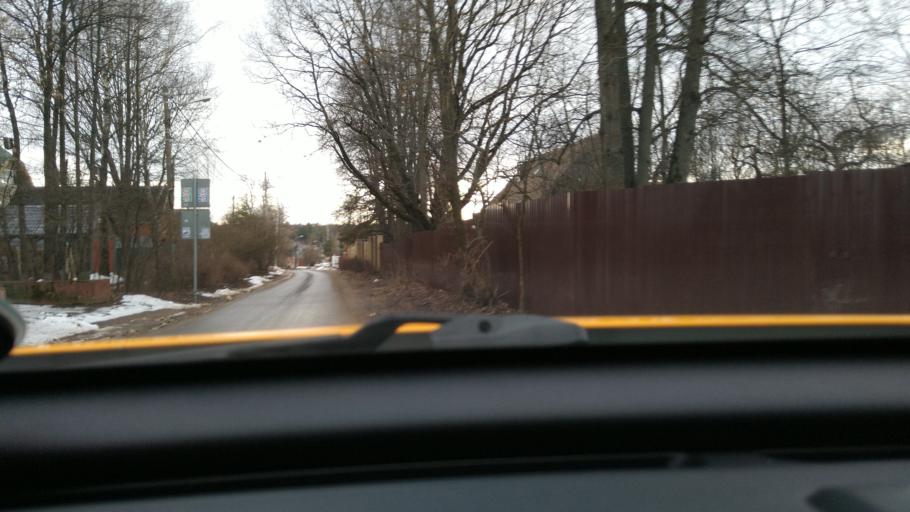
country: RU
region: Moskovskaya
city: Petrovo-Dal'neye
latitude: 55.7720
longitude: 37.1979
